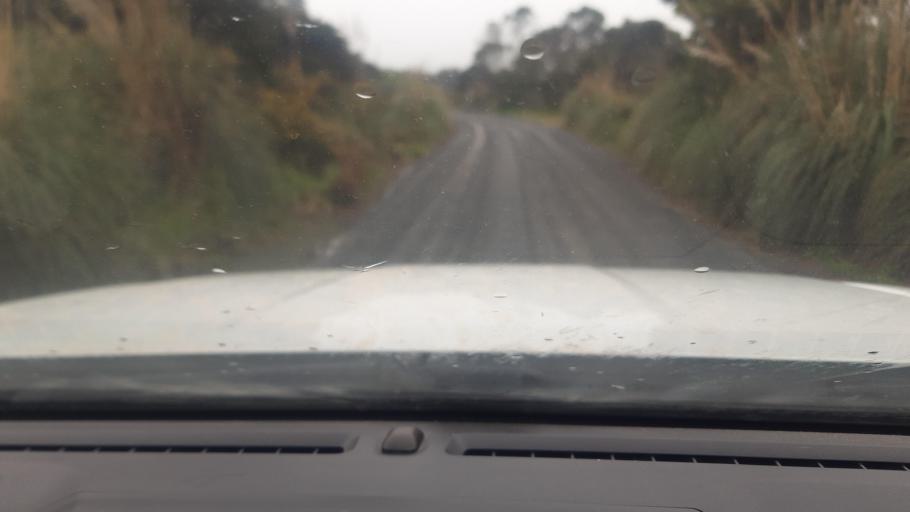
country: NZ
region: Northland
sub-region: Far North District
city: Kaitaia
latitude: -34.9091
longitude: 173.2702
